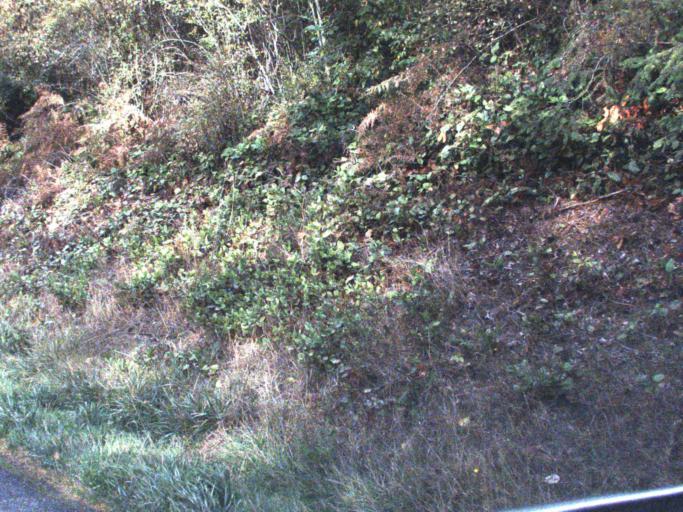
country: US
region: Washington
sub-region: Island County
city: Coupeville
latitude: 48.1757
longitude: -122.6166
